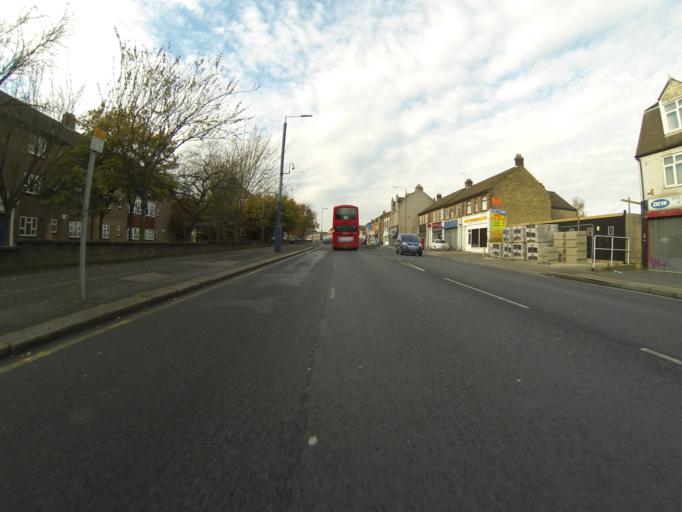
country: GB
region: England
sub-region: Greater London
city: Welling
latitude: 51.4615
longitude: 0.1146
